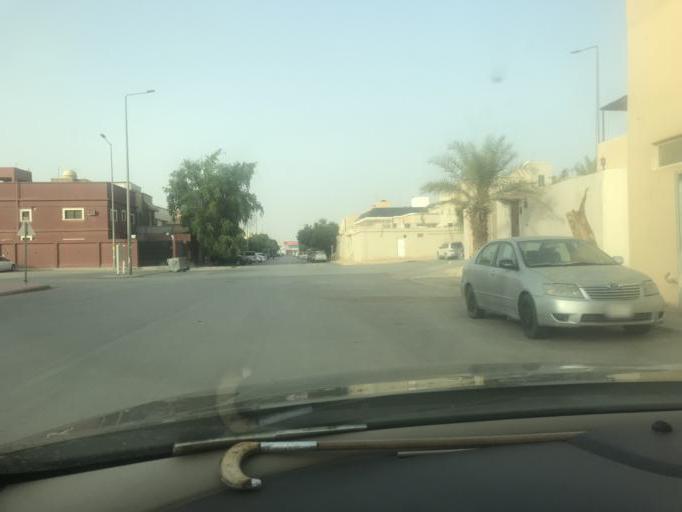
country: SA
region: Ar Riyad
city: Riyadh
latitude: 24.7429
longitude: 46.7732
